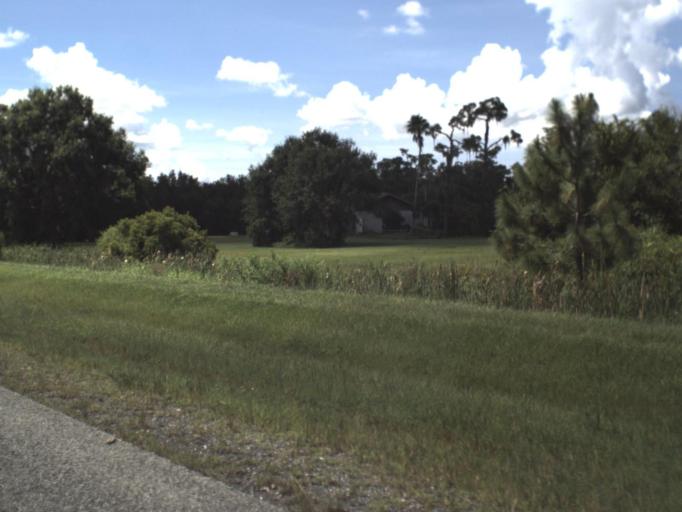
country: US
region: Florida
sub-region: Charlotte County
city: Harbour Heights
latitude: 27.0019
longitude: -81.9589
